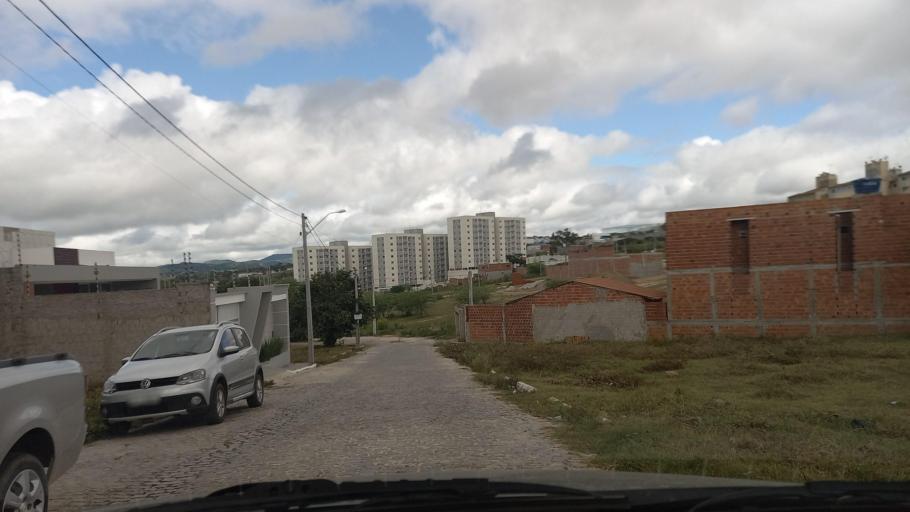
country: BR
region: Pernambuco
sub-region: Caruaru
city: Caruaru
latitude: -8.3022
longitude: -35.9568
